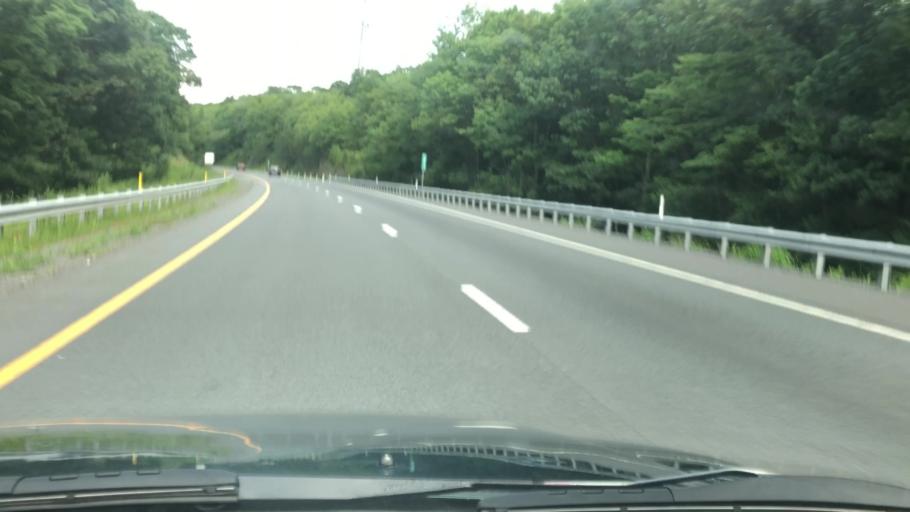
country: US
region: Pennsylvania
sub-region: Pike County
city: Conashaugh Lakes
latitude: 41.3458
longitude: -74.9952
